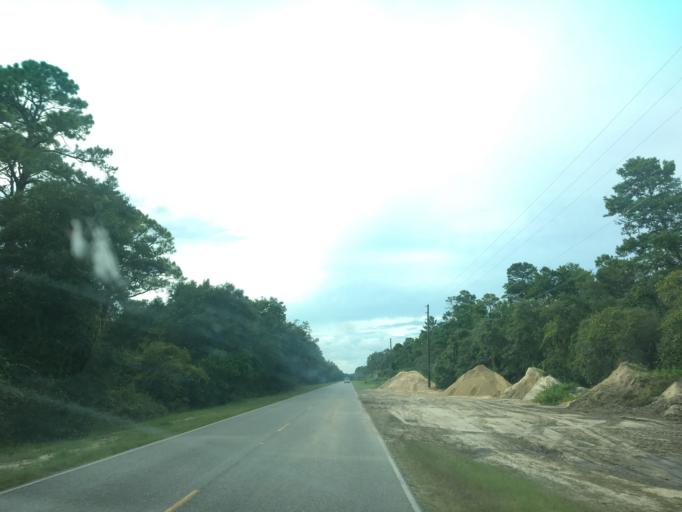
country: US
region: Florida
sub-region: Wakulla County
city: Crawfordville
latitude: 29.9171
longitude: -84.3695
